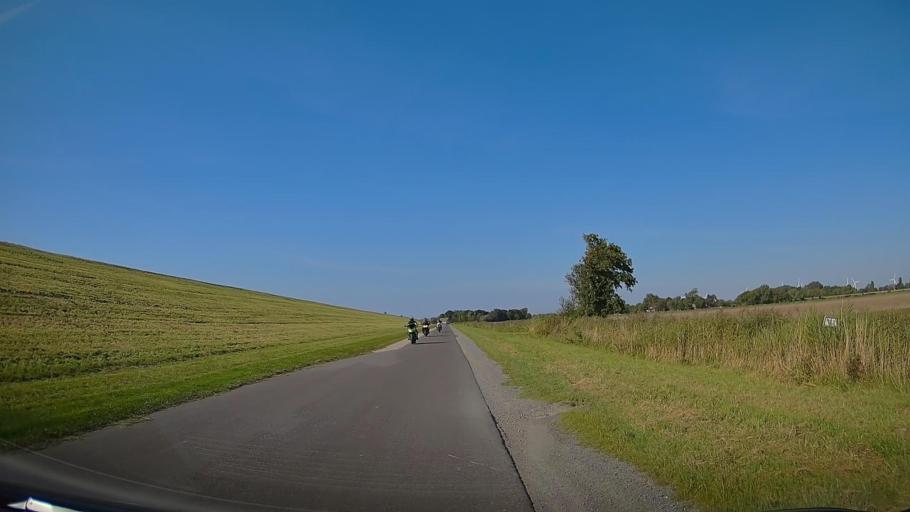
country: DE
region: Lower Saxony
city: Wremen
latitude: 53.6519
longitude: 8.4944
